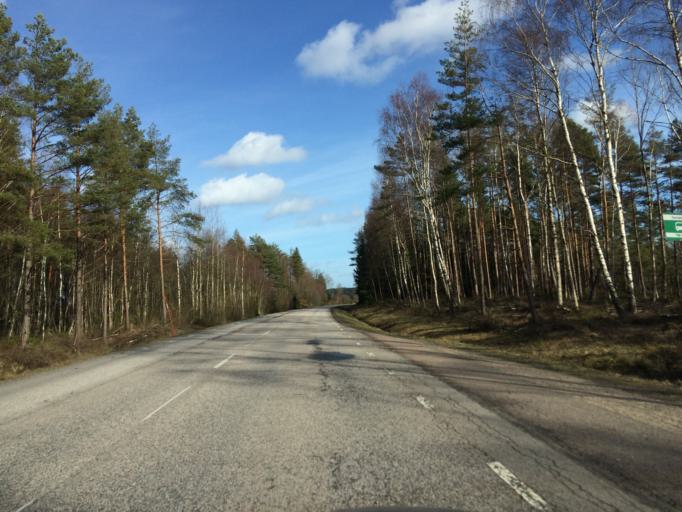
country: SE
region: Halland
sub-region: Hylte Kommun
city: Hyltebruk
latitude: 56.8226
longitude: 13.5080
